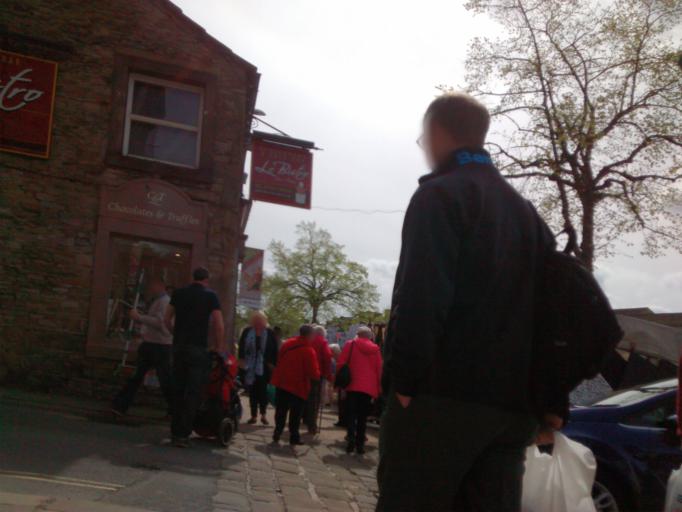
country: GB
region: England
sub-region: North Yorkshire
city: Skipton
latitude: 53.9624
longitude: -2.0161
